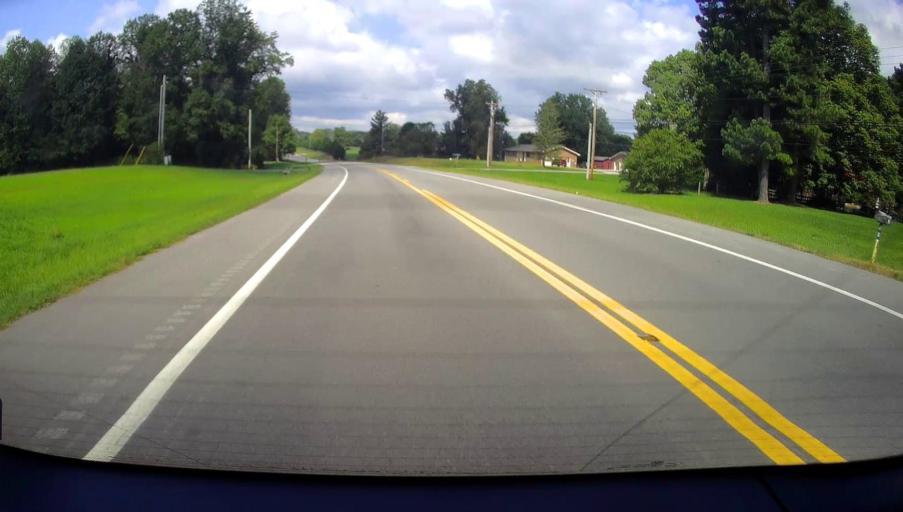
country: US
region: Tennessee
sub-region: Coffee County
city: New Union
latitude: 35.5154
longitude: -86.1300
